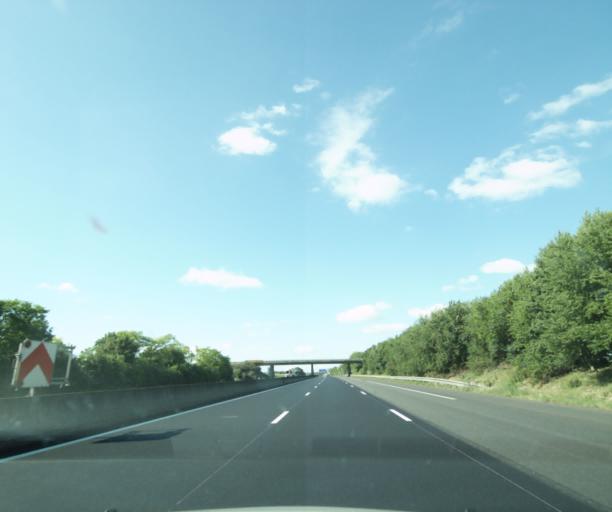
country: FR
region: Centre
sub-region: Departement du Loiret
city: Artenay
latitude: 48.0771
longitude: 1.8505
